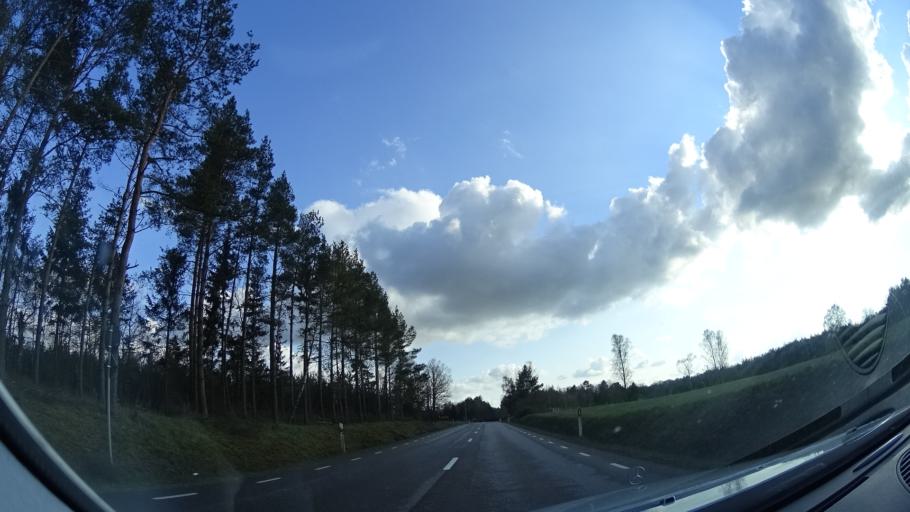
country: SE
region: Skane
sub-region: Klippans Kommun
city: Ljungbyhed
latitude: 56.0907
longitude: 13.2808
